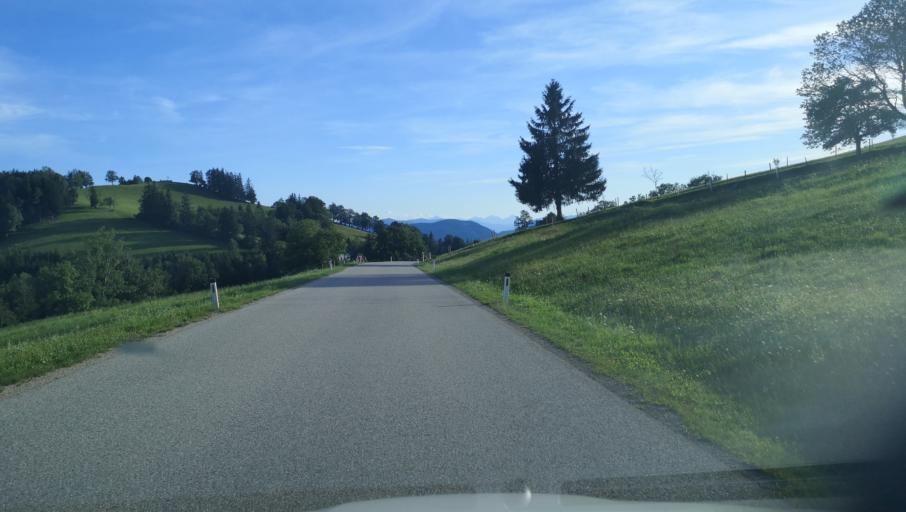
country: AT
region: Lower Austria
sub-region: Politischer Bezirk Amstetten
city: Neuhofen an der Ybbs
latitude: 47.9927
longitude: 14.8563
